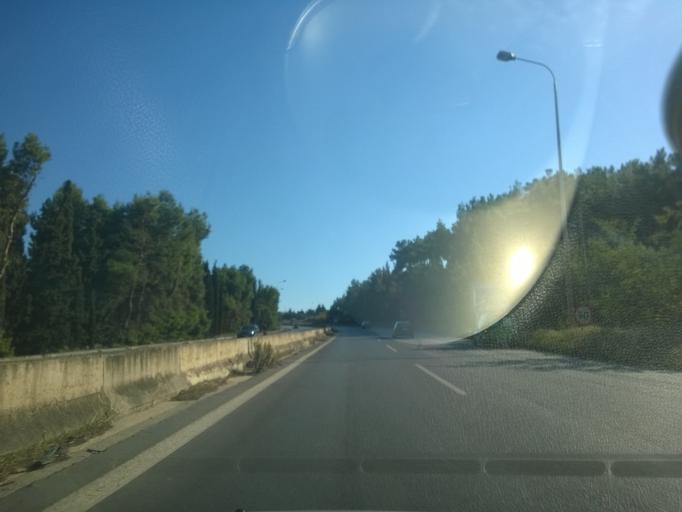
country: GR
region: Central Macedonia
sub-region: Nomos Thessalonikis
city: Kardia
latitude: 40.4613
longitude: 22.9985
